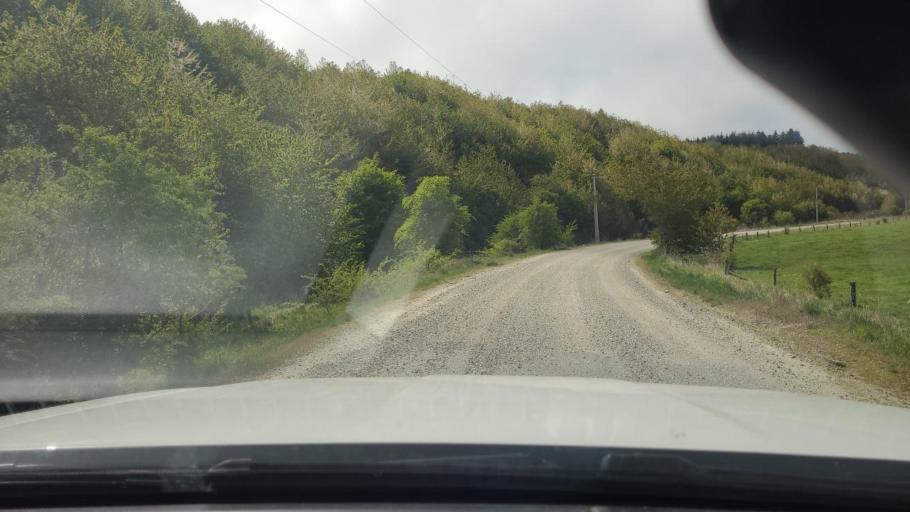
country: NZ
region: Southland
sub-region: Gore District
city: Gore
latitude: -45.7246
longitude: 168.8585
